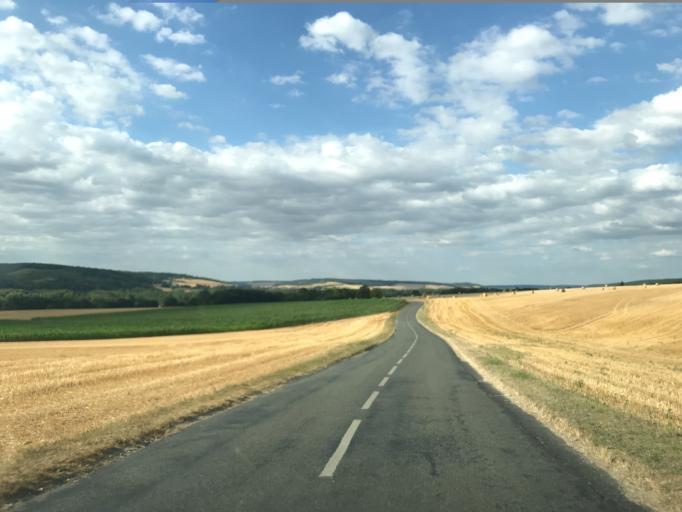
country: FR
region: Ile-de-France
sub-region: Departement des Yvelines
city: Freneuse
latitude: 49.0677
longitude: 1.5895
